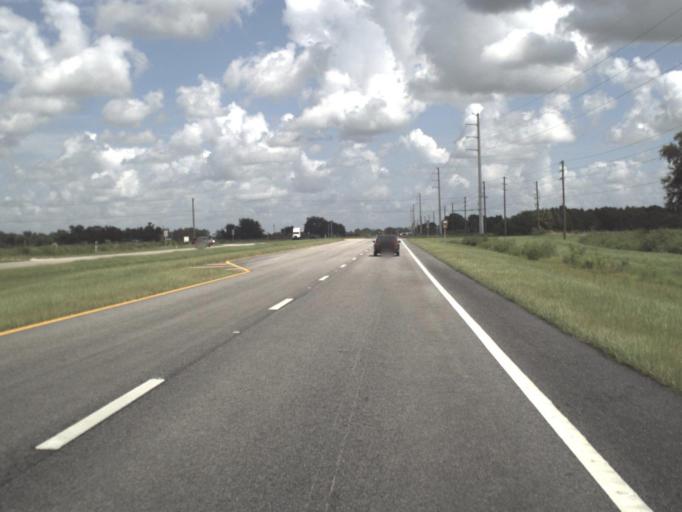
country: US
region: Florida
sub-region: Charlotte County
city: Harbour Heights
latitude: 27.0659
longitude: -81.9580
